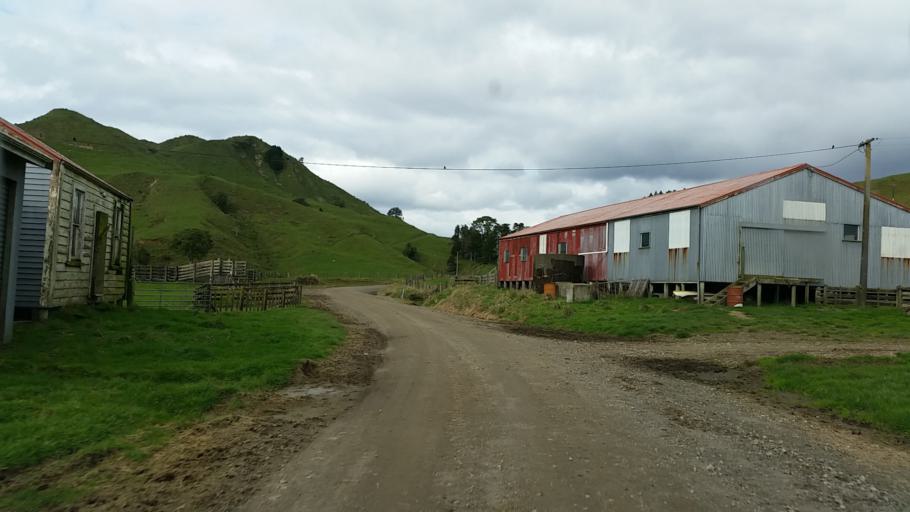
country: NZ
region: Taranaki
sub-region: New Plymouth District
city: Waitara
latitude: -39.1609
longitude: 174.5946
